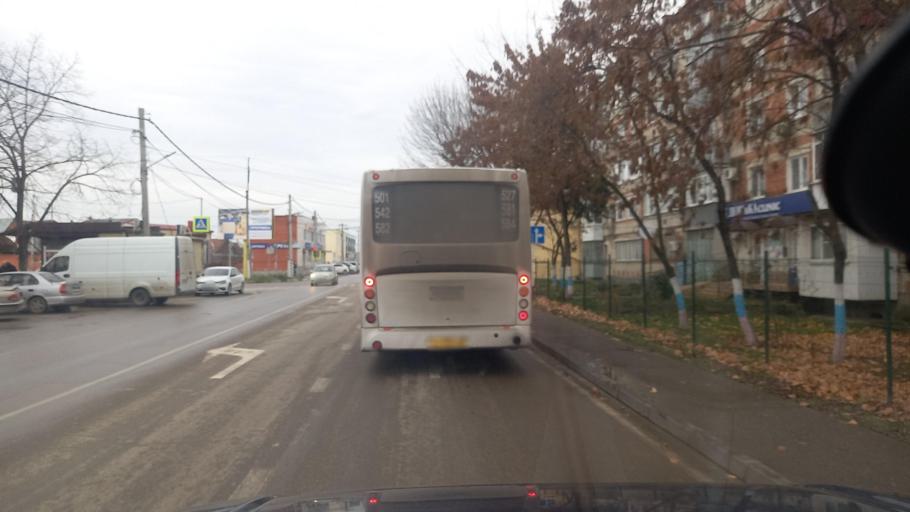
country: RU
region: Adygeya
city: Yablonovskiy
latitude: 44.9798
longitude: 38.9369
